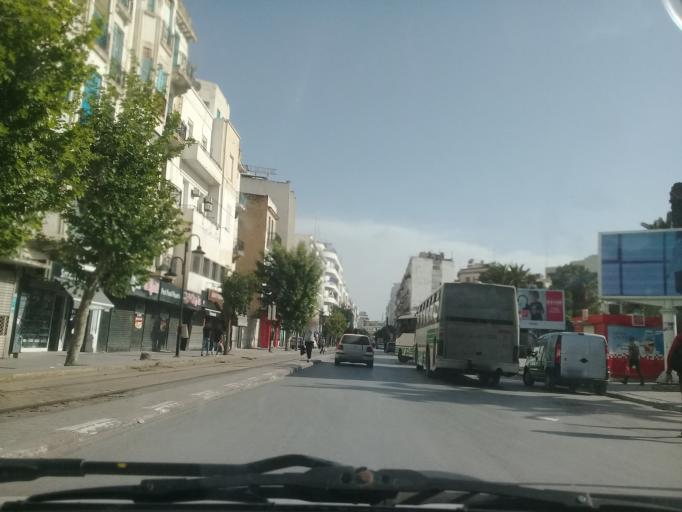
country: TN
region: Tunis
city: Tunis
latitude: 36.8054
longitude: 10.1803
